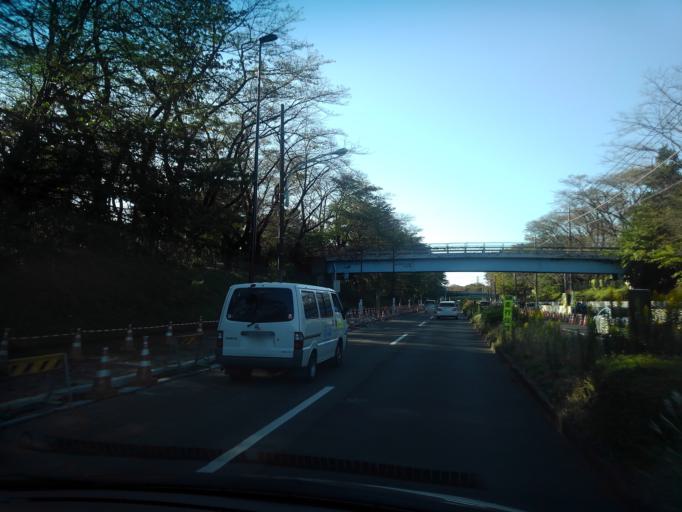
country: JP
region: Tokyo
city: Chofugaoka
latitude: 35.6844
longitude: 139.5252
